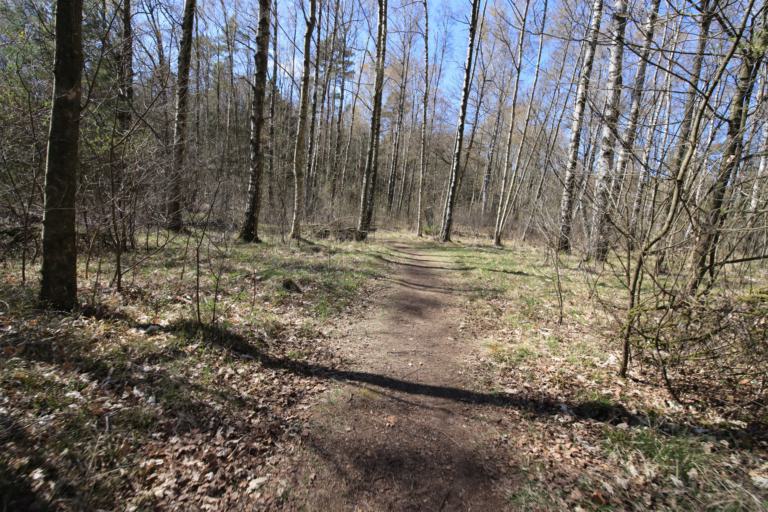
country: SE
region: Halland
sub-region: Varbergs Kommun
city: Varberg
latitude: 57.1802
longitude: 12.2374
